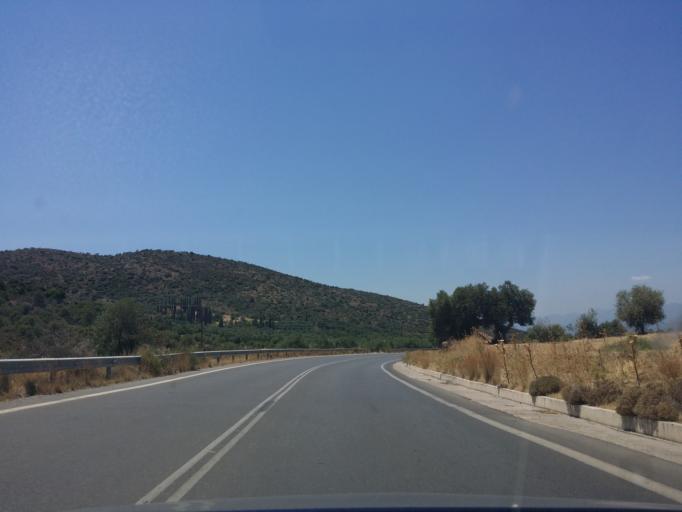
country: GR
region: Peloponnese
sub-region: Nomos Lakonias
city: Kato Glikovrisi
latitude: 36.8645
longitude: 22.8063
